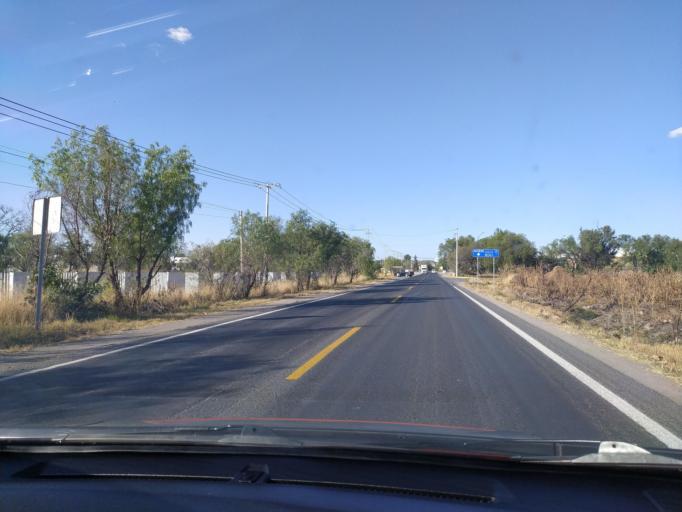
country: LA
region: Oudomxai
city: Muang La
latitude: 21.0232
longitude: 101.8259
